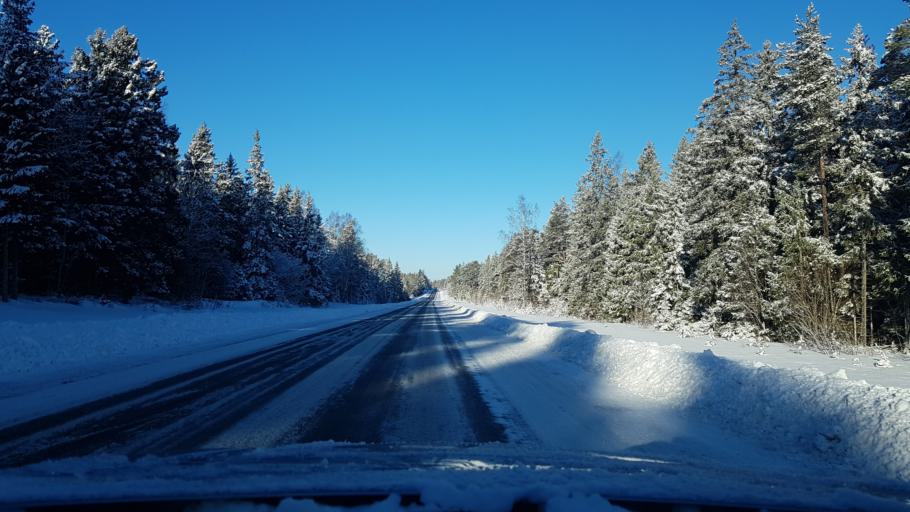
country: EE
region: Hiiumaa
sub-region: Kaerdla linn
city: Kardla
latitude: 58.9665
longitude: 22.8333
